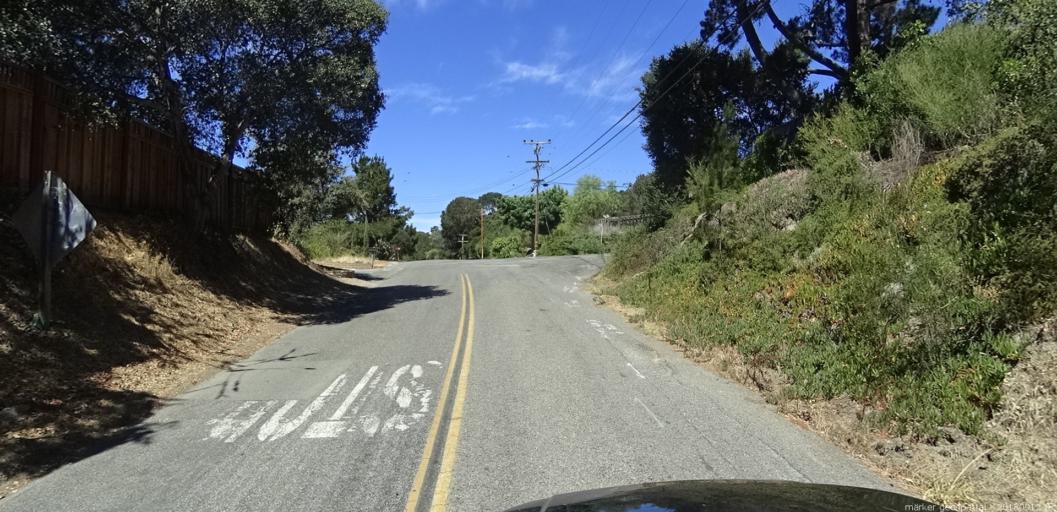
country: US
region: California
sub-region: Monterey County
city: Carmel Valley Village
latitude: 36.4859
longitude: -121.7375
